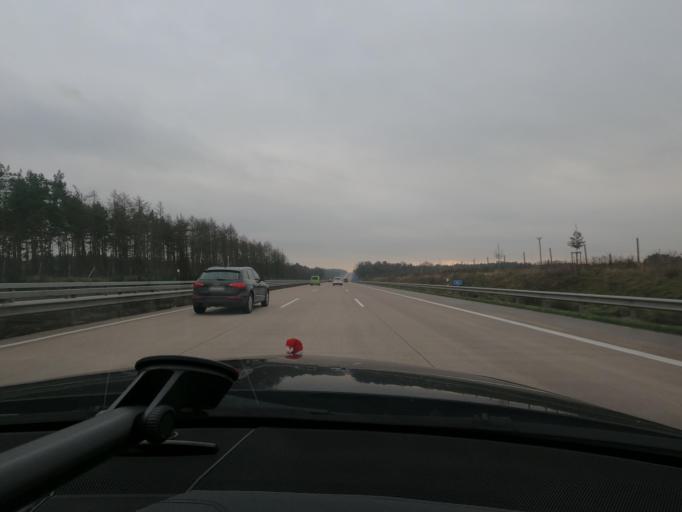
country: DE
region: Lower Saxony
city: Bad Fallingbostel
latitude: 52.8219
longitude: 9.6835
